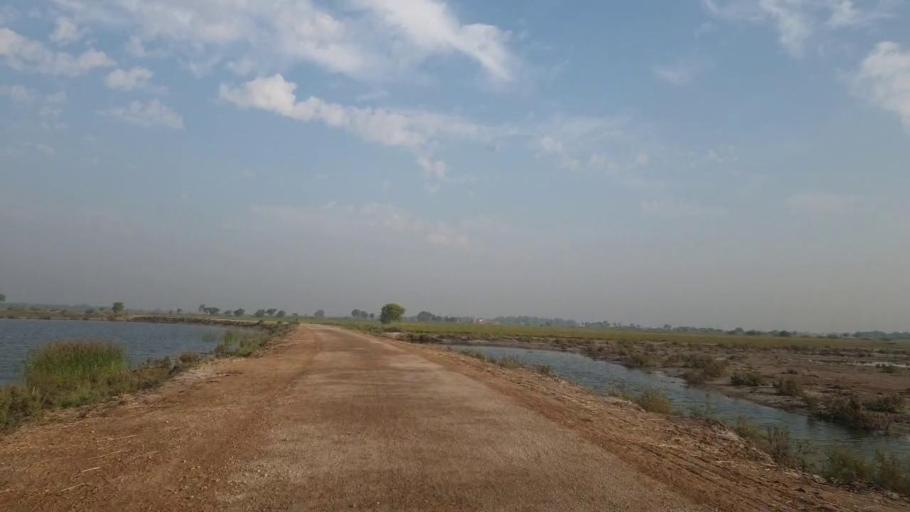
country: PK
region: Sindh
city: Tando Bago
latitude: 24.8138
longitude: 68.9564
